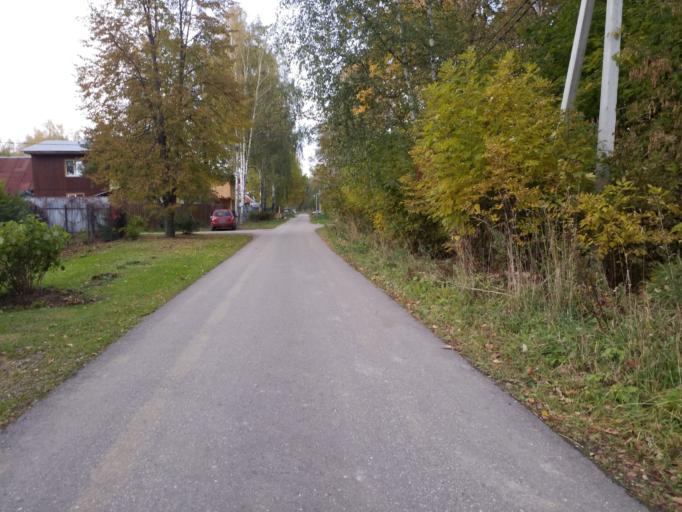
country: RU
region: Moskovskaya
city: Ashukino
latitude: 56.1656
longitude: 37.9537
